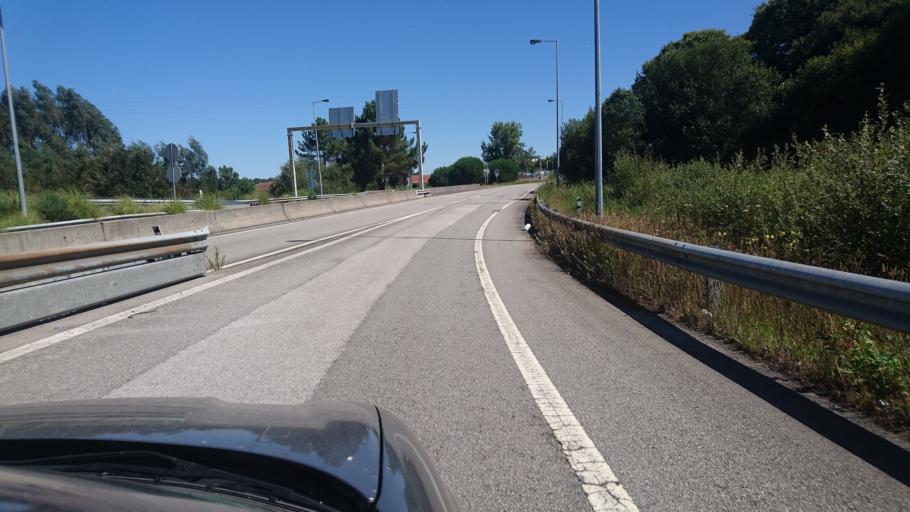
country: PT
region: Aveiro
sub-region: Santa Maria da Feira
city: Rio Meao
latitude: 40.9250
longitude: -8.5793
